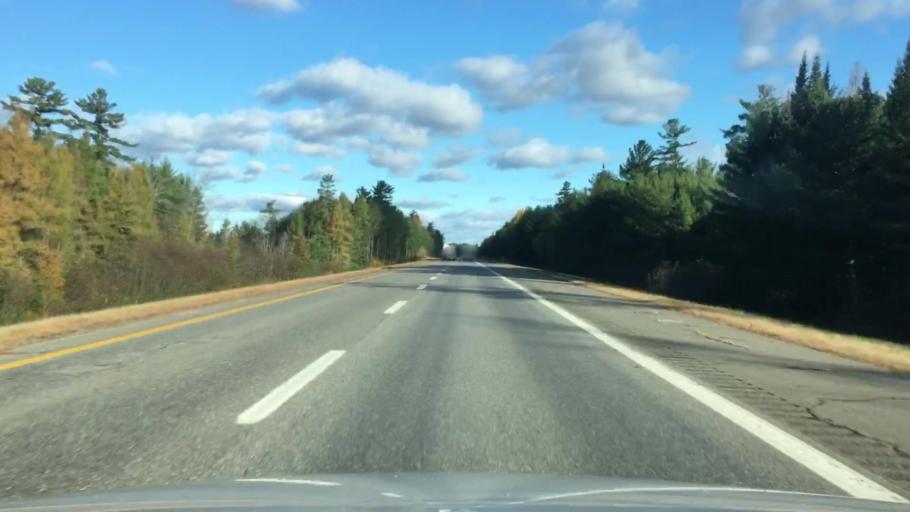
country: US
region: Maine
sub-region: Penobscot County
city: Greenbush
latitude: 45.1342
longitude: -68.6981
